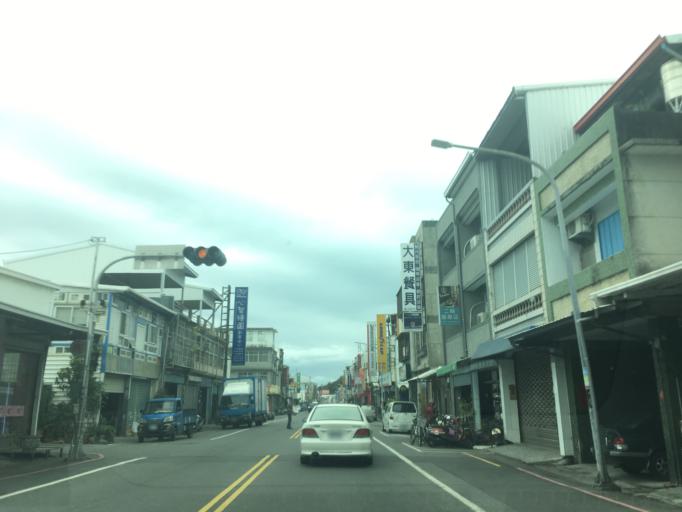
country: TW
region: Taiwan
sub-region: Taitung
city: Taitung
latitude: 22.7629
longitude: 121.1366
